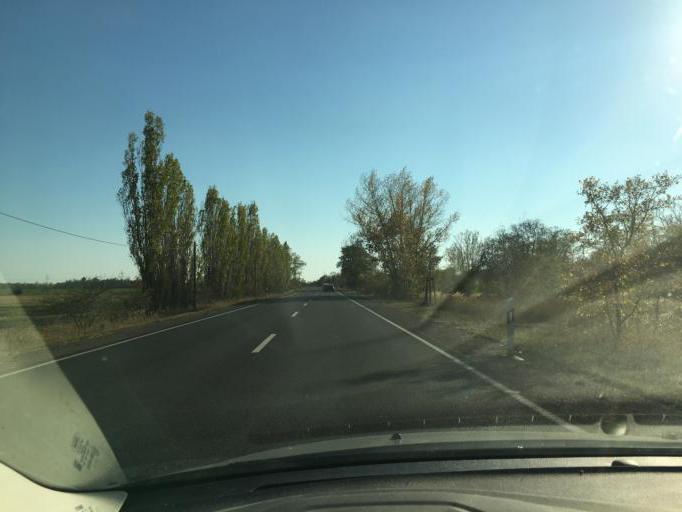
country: DE
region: Saxony-Anhalt
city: Zscherndorf
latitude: 51.5919
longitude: 12.2789
